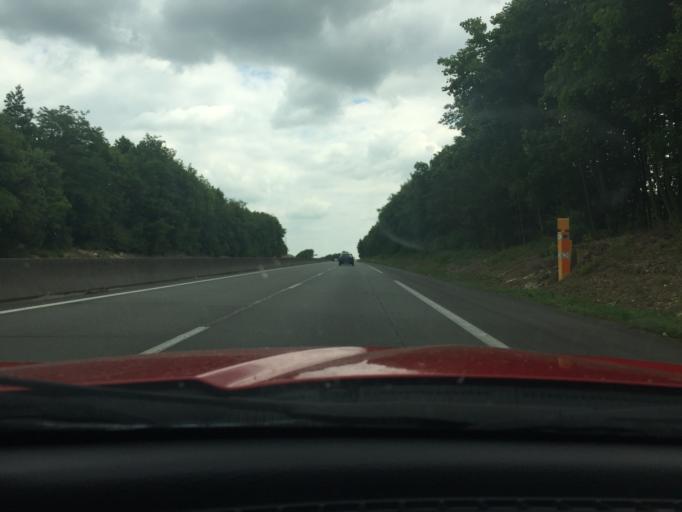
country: FR
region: Picardie
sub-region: Departement de l'Aisne
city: Couvron-et-Aumencourt
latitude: 49.6641
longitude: 3.5327
